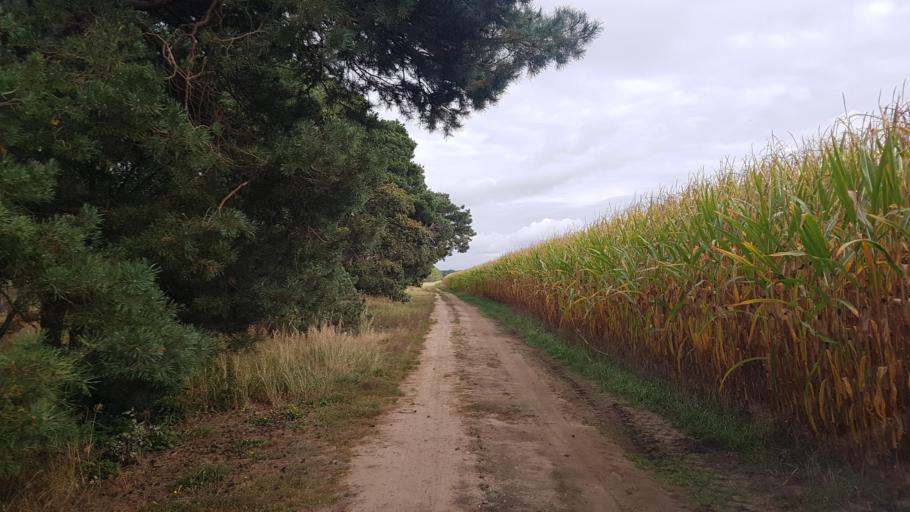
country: DE
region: Brandenburg
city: Bad Liebenwerda
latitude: 51.4741
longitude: 13.4364
